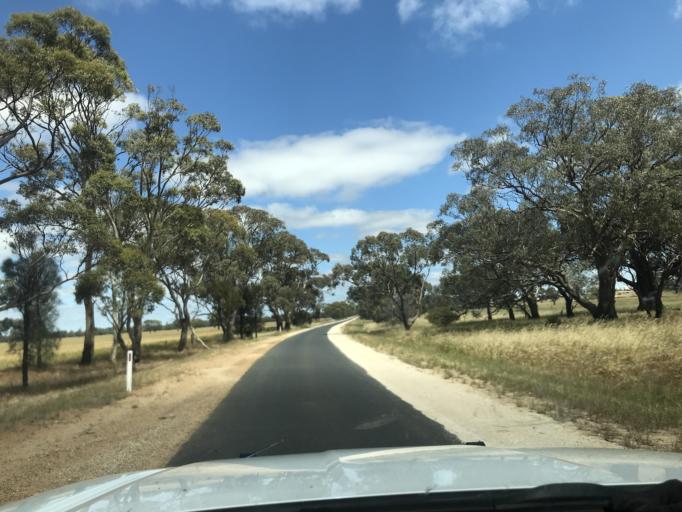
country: AU
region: South Australia
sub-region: Tatiara
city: Bordertown
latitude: -36.3085
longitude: 141.0536
